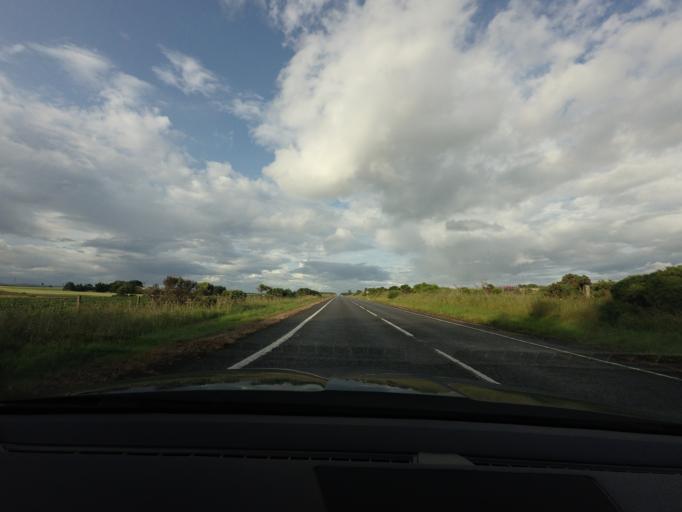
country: GB
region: Scotland
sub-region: Highland
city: Fortrose
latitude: 57.5401
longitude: -4.0160
